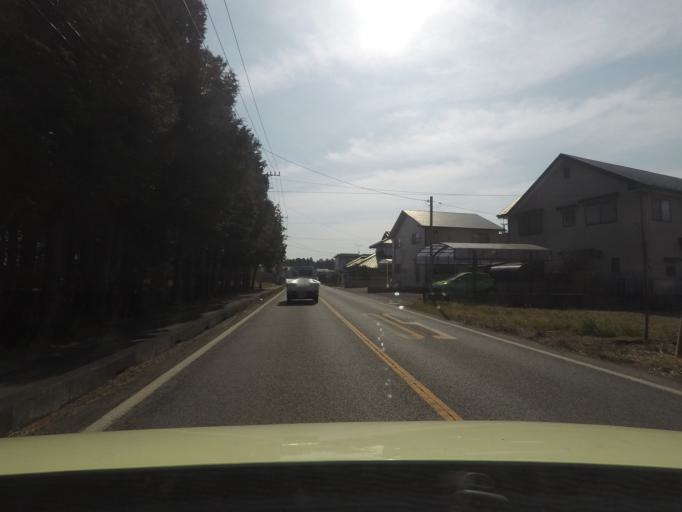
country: JP
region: Ibaraki
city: Naka
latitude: 36.0729
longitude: 140.1507
